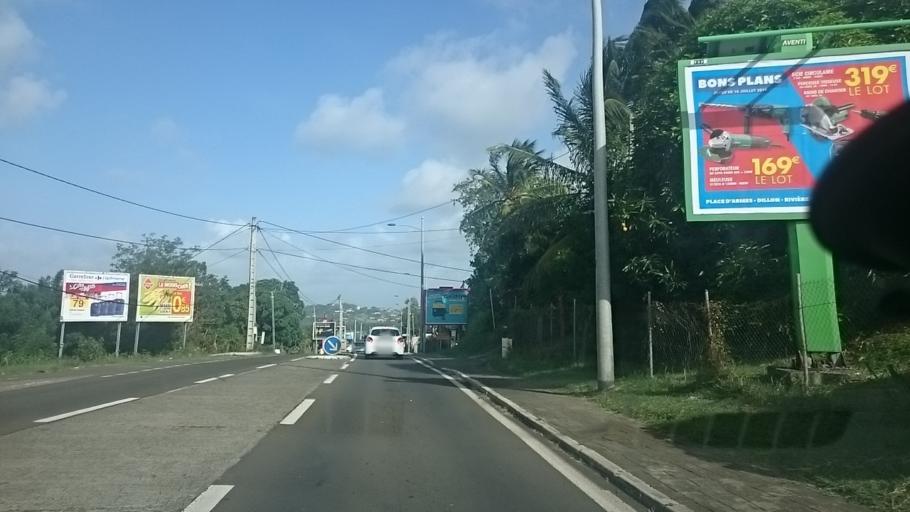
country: MQ
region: Martinique
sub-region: Martinique
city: Le Francois
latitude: 14.6025
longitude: -60.8766
